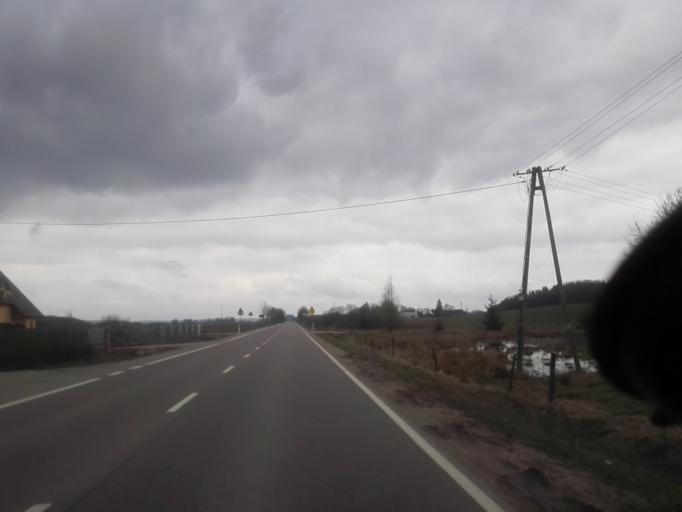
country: PL
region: Podlasie
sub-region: Suwalki
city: Suwalki
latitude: 54.2110
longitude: 22.9125
